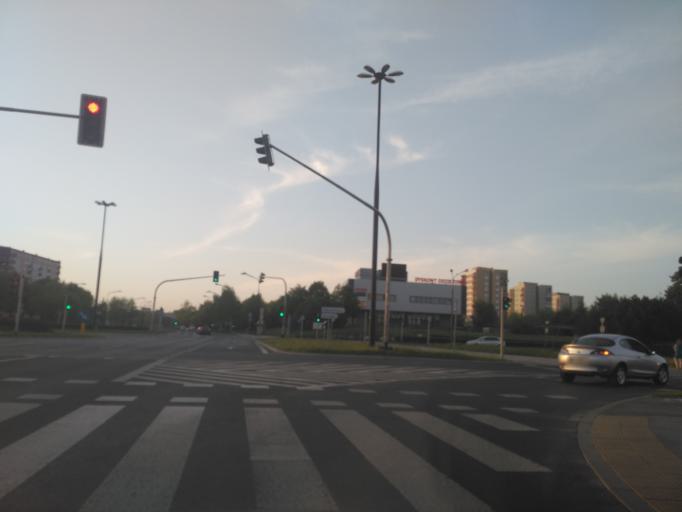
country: PL
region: Lublin Voivodeship
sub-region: Powiat lubelski
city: Lublin
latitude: 51.2621
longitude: 22.5523
